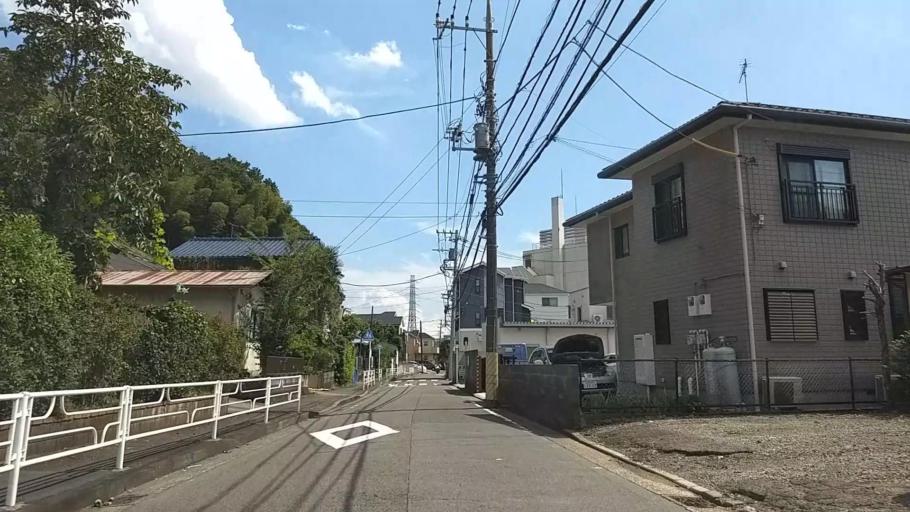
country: JP
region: Kanagawa
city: Yokohama
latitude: 35.5203
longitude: 139.5797
